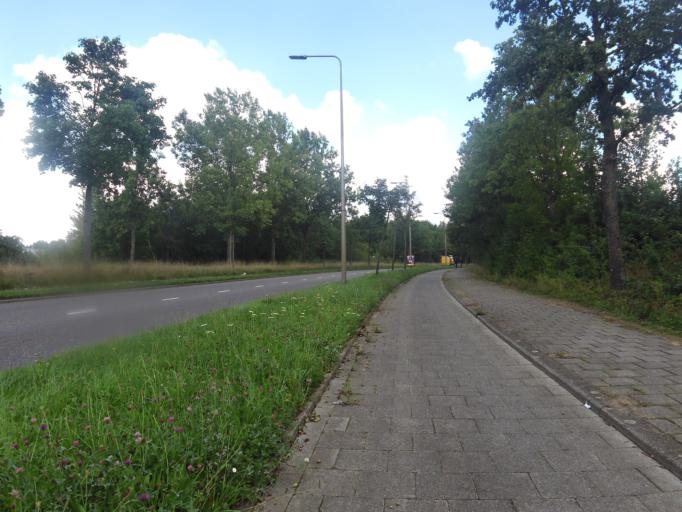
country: NL
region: Limburg
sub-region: Gemeente Heerlen
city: Nieuw-Lotbroek
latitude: 50.9124
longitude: 5.9454
